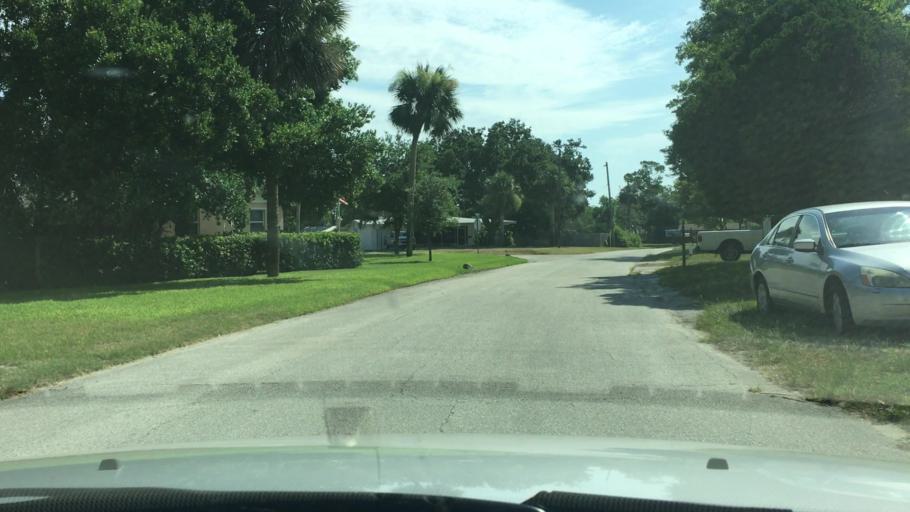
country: US
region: Florida
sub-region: Volusia County
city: Holly Hill
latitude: 29.2601
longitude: -81.0459
